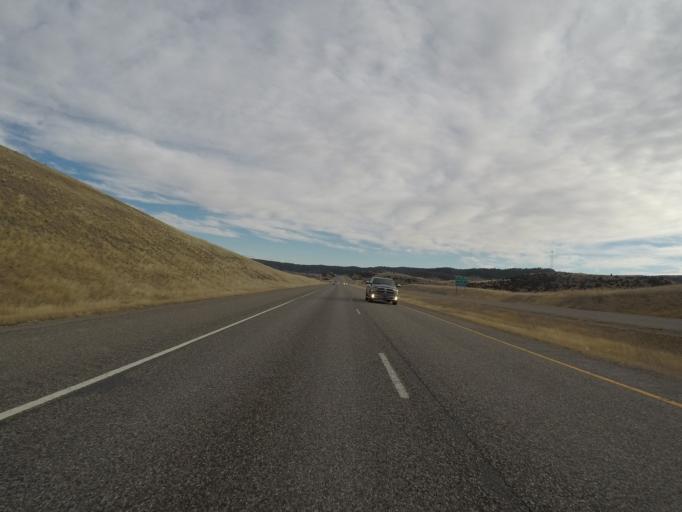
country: US
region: Montana
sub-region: Stillwater County
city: Absarokee
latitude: 45.6867
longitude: -109.4680
